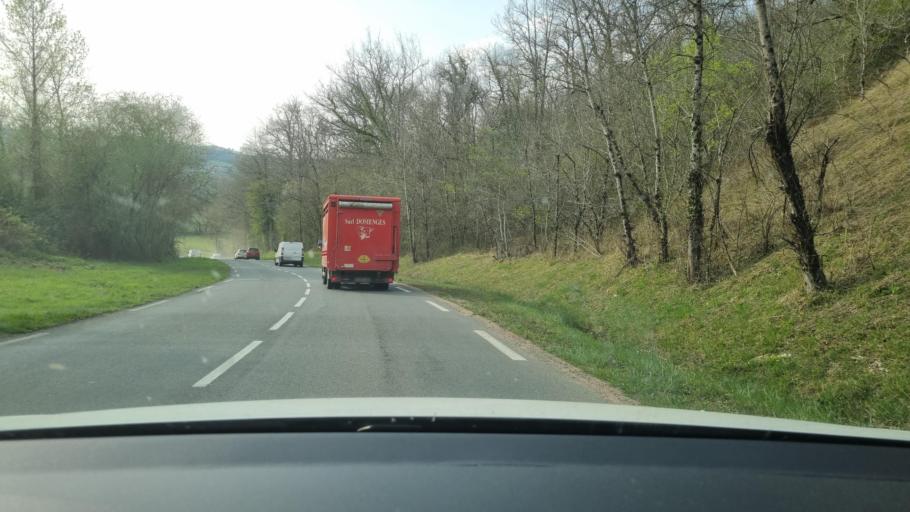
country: FR
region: Aquitaine
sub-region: Departement des Pyrenees-Atlantiques
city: Soumoulou
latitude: 43.3763
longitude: -0.1079
